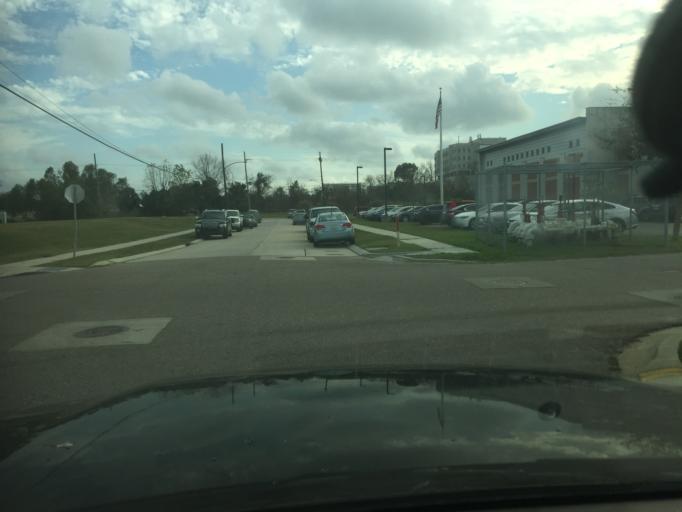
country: US
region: Louisiana
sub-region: Orleans Parish
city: New Orleans
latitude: 29.9946
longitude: -90.0829
